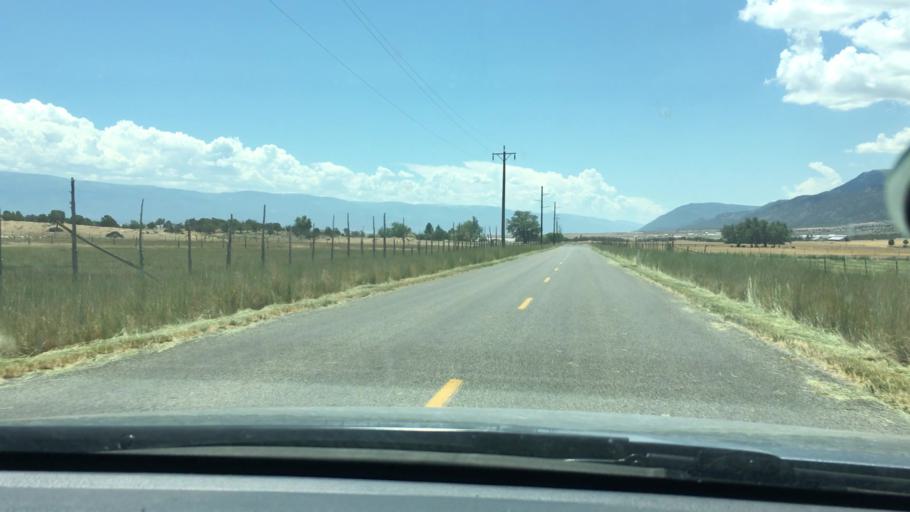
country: US
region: Utah
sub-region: Sanpete County
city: Fountain Green
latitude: 39.6052
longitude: -111.6438
